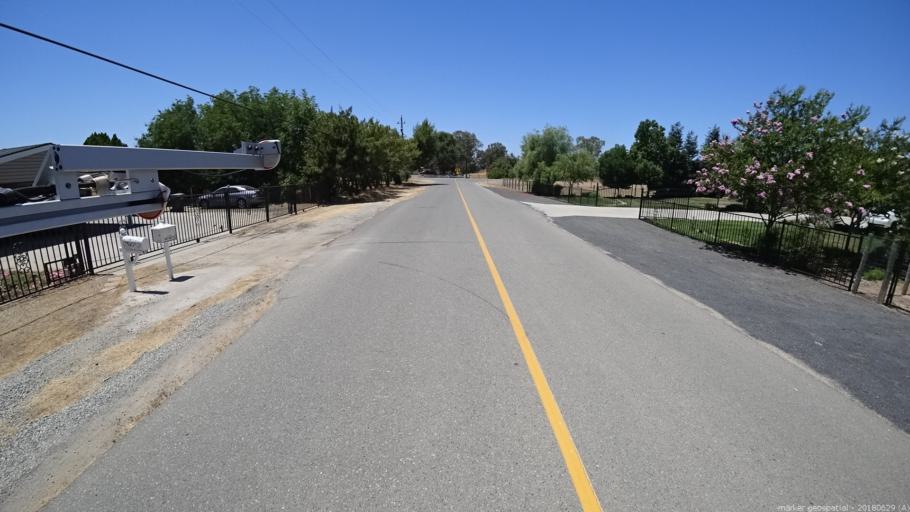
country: US
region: California
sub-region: Madera County
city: Parksdale
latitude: 36.9930
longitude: -119.9905
